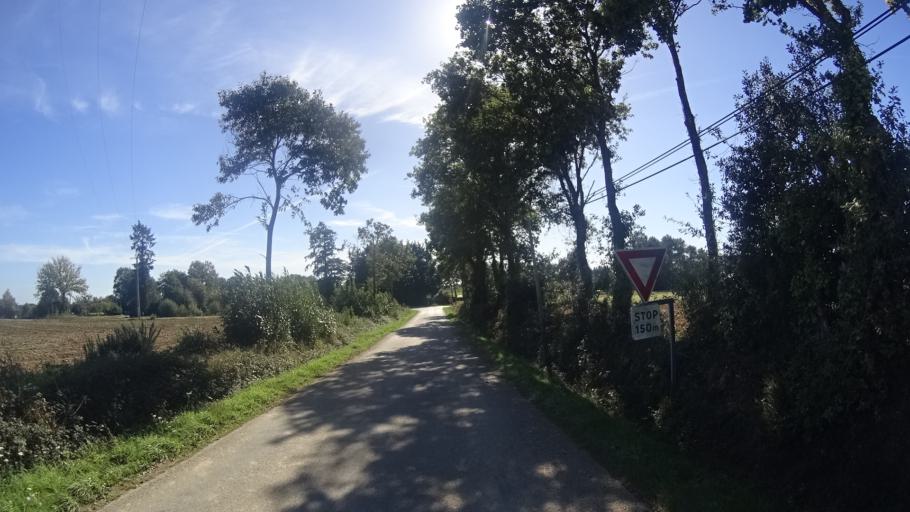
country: FR
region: Brittany
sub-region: Departement du Morbihan
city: Peillac
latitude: 47.7484
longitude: -2.2066
